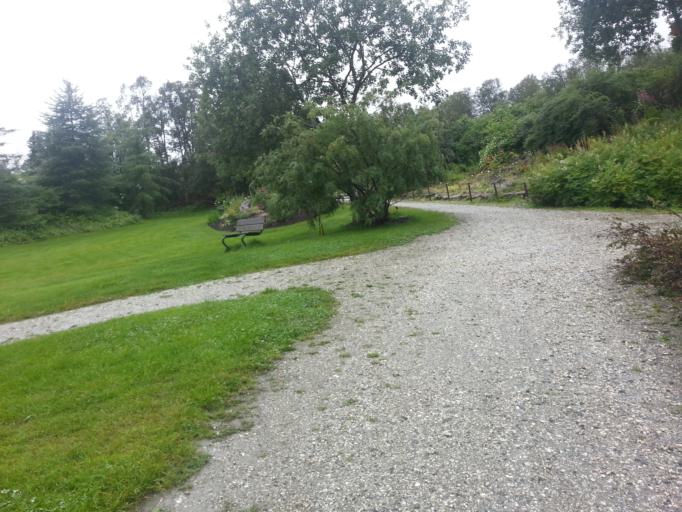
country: NO
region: Troms
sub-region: Tromso
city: Tromso
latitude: 69.6767
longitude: 18.9745
